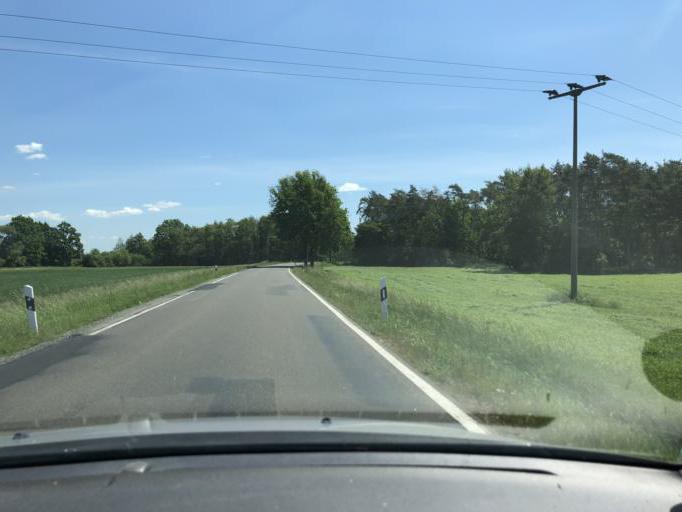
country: DE
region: Saxony
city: Trebsen
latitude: 51.2918
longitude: 12.7353
